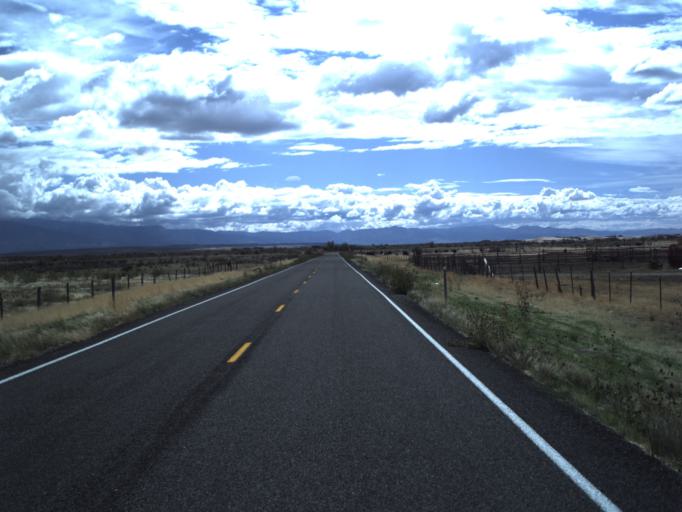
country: US
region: Utah
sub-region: Millard County
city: Fillmore
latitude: 39.1416
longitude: -112.4098
